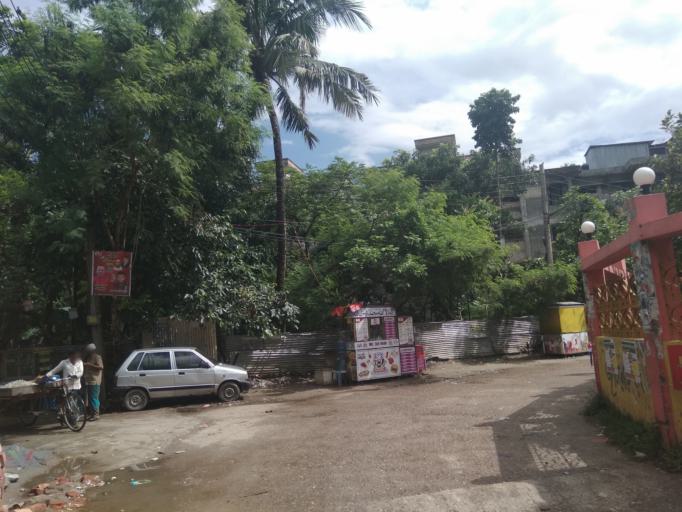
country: BD
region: Dhaka
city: Azimpur
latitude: 23.7994
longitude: 90.3832
